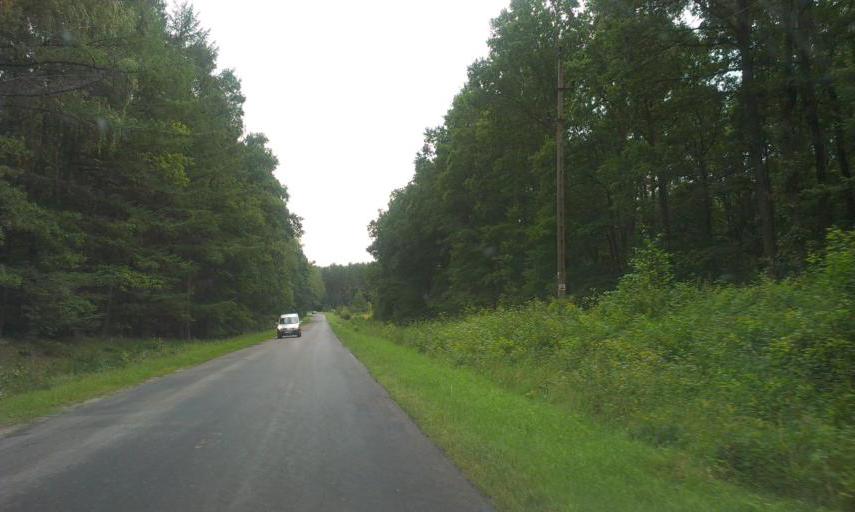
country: PL
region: West Pomeranian Voivodeship
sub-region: Powiat swidwinski
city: Polczyn-Zdroj
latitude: 53.7853
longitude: 16.1404
